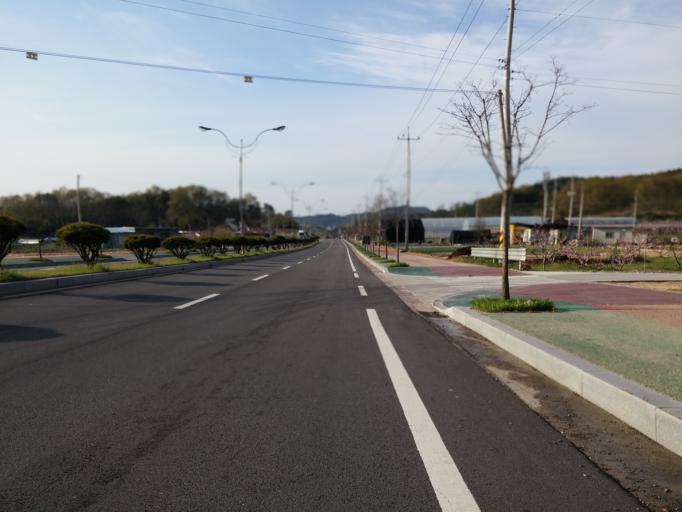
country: KR
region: Chungcheongbuk-do
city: Okcheon
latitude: 36.2912
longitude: 127.5862
